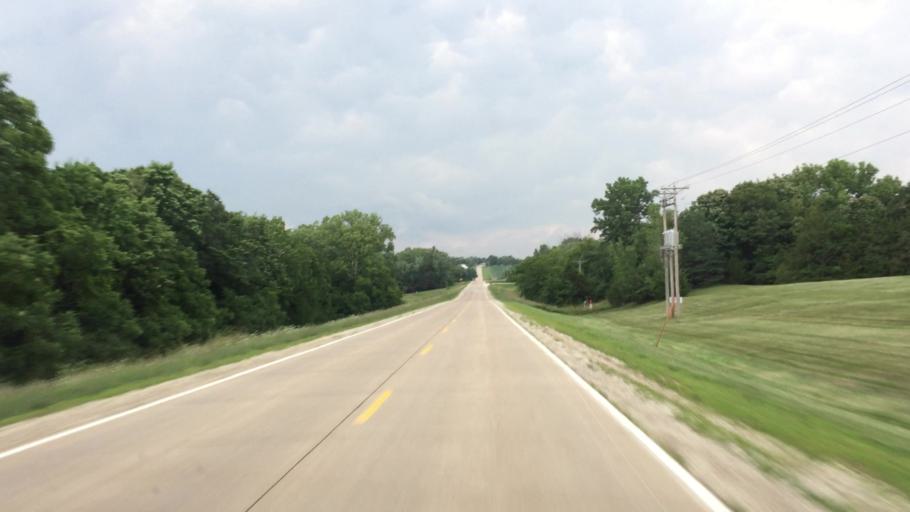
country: US
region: Iowa
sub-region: Lee County
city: Fort Madison
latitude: 40.7142
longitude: -91.3300
